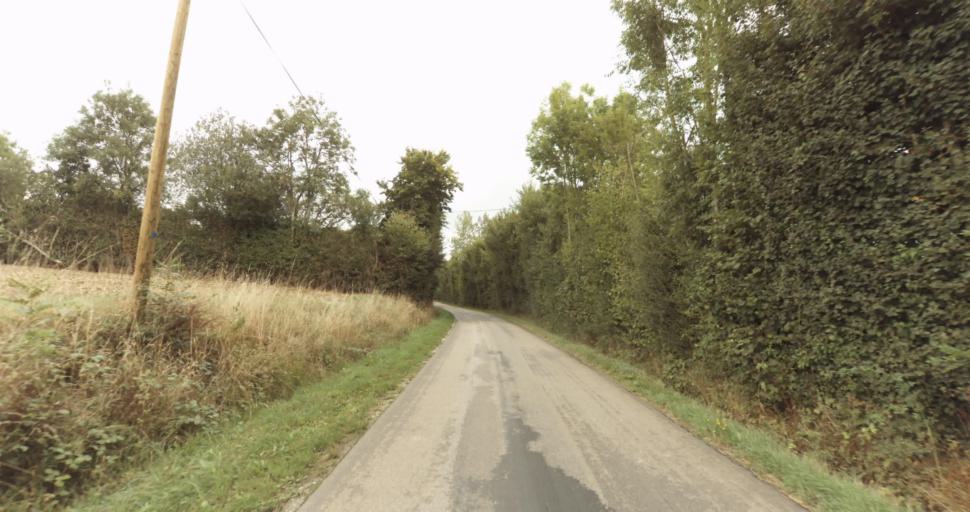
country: FR
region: Lower Normandy
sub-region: Departement de l'Orne
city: Sainte-Gauburge-Sainte-Colombe
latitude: 48.7052
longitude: 0.3589
